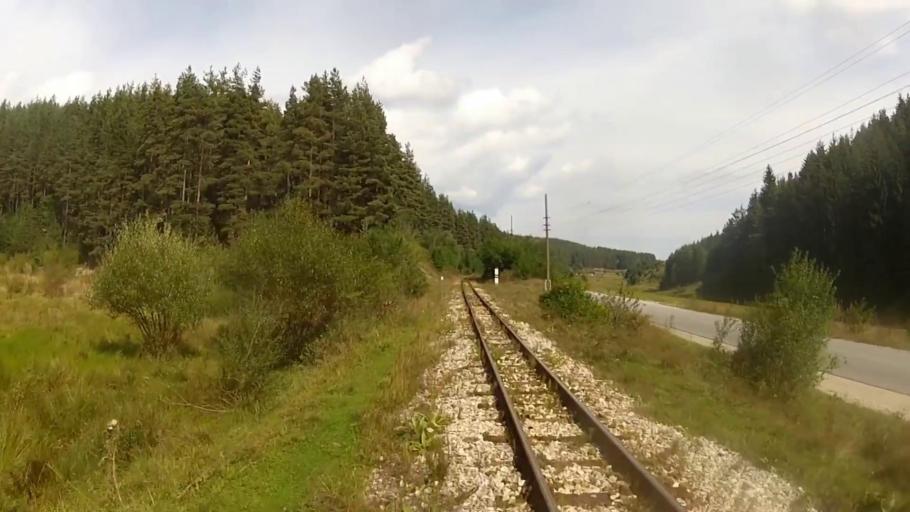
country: BG
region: Blagoevgrad
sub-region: Obshtina Yakoruda
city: Yakoruda
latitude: 42.0372
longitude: 23.8067
